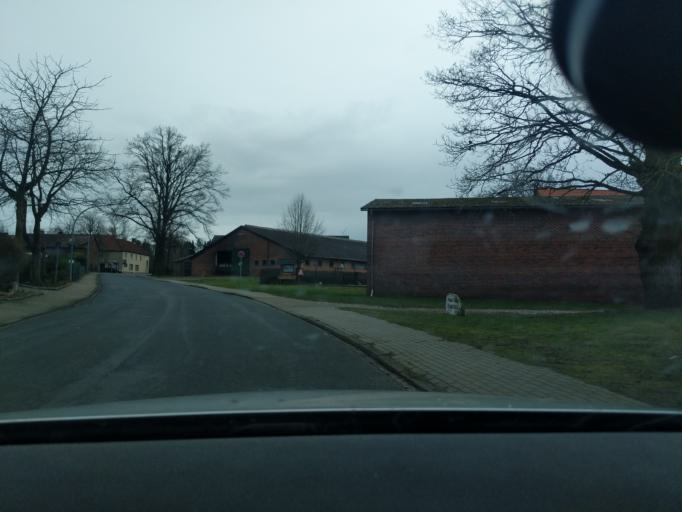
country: DE
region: Lower Saxony
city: Bremervorde
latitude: 53.4663
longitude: 9.1983
